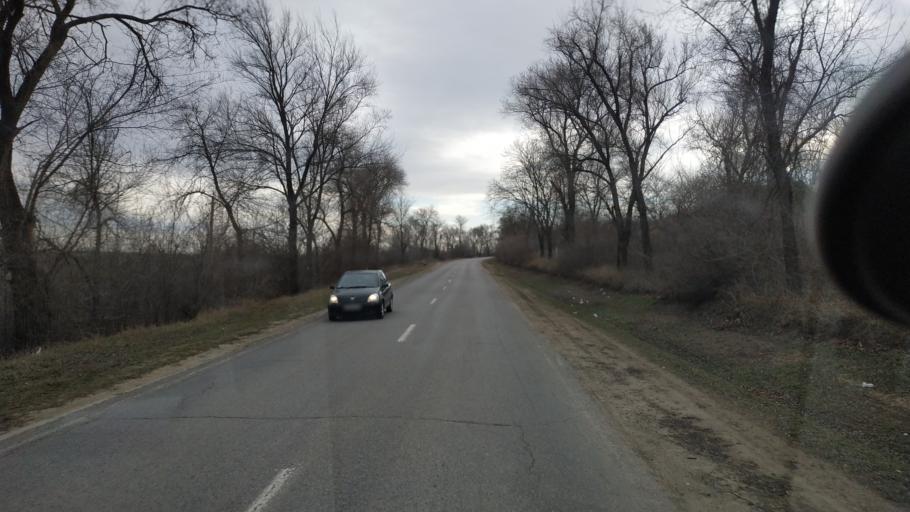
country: MD
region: Chisinau
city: Vadul lui Voda
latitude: 47.1276
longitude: 29.0630
